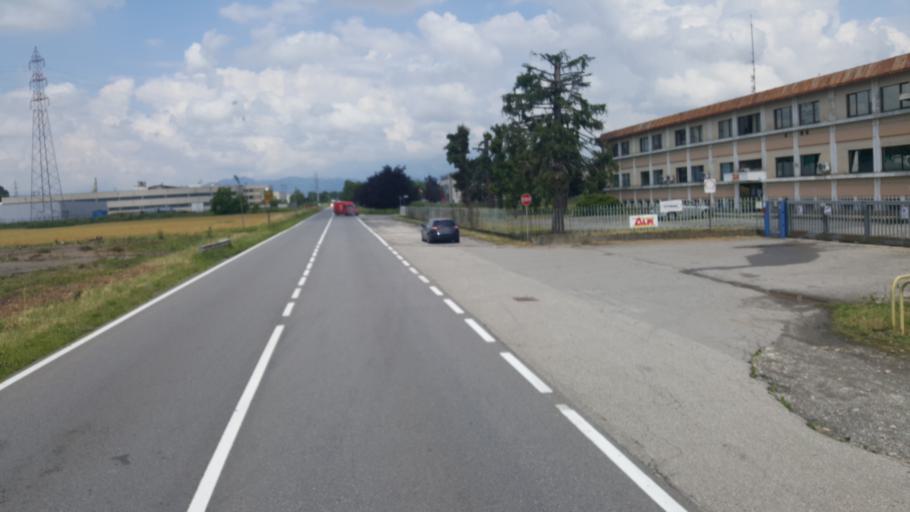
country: IT
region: Lombardy
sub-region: Provincia di Bergamo
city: Grignano
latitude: 45.6283
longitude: 9.5479
